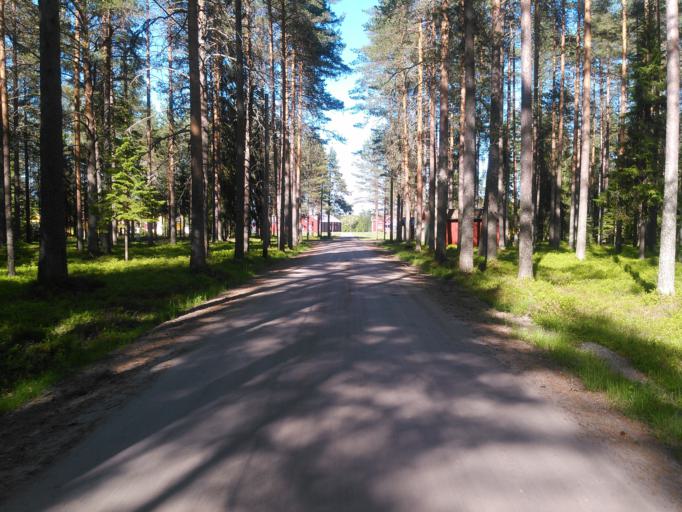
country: SE
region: Vaesterbotten
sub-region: Umea Kommun
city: Roback
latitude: 63.8327
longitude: 20.1113
